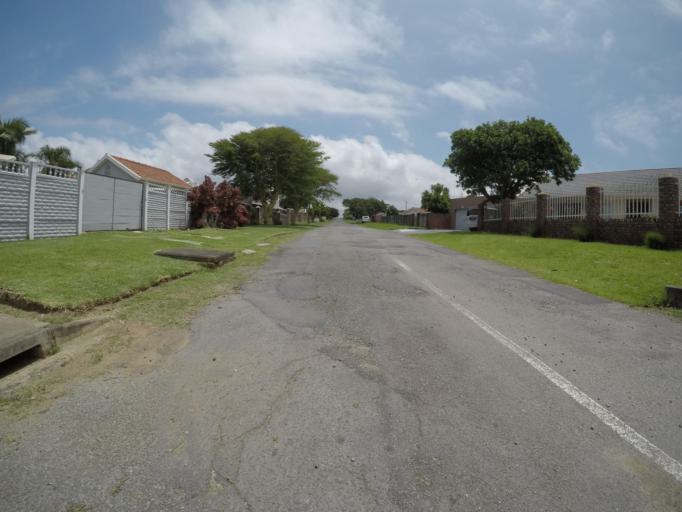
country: ZA
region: Eastern Cape
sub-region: Buffalo City Metropolitan Municipality
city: East London
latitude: -32.9420
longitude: 28.0170
